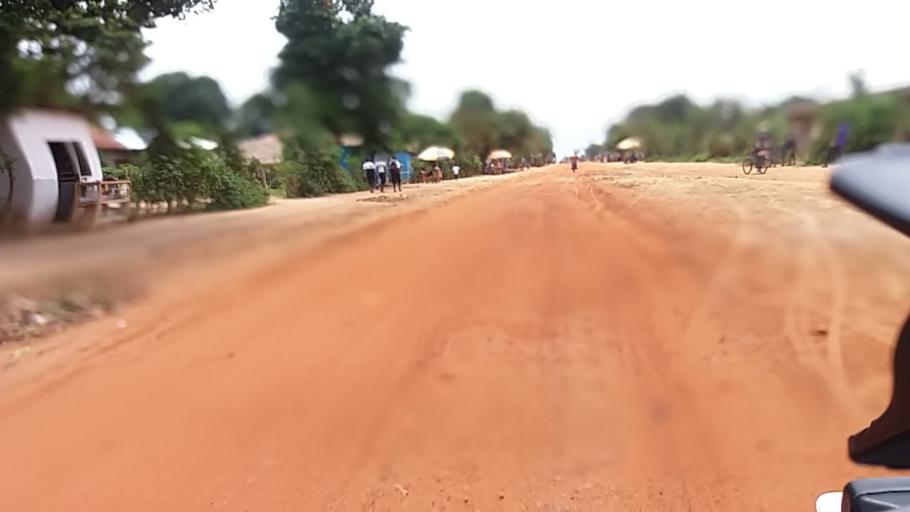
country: CD
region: Bandundu
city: Bandundu
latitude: -3.3208
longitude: 17.3948
